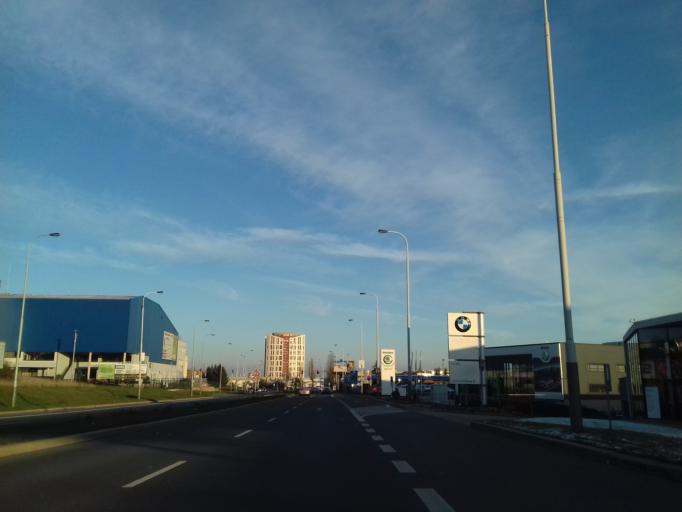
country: CZ
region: Central Bohemia
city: Trebotov
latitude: 50.0398
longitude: 14.3257
